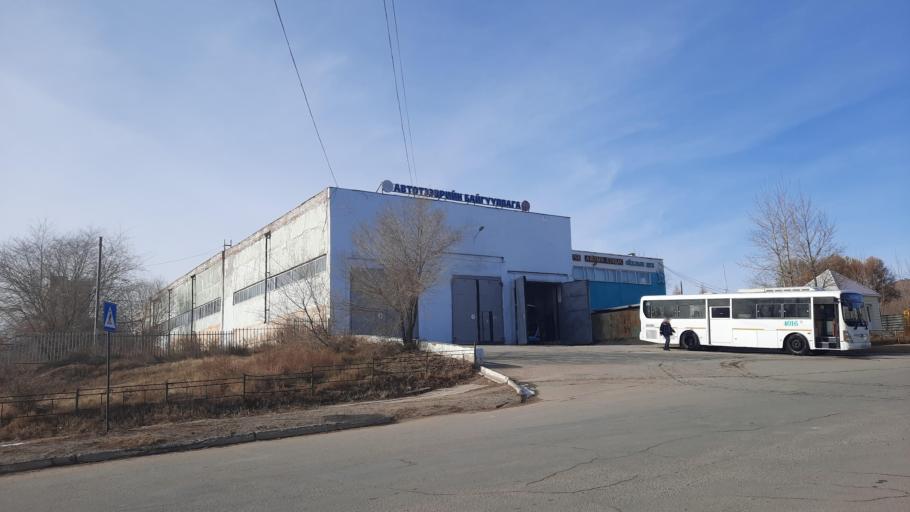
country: MN
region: Orhon
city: Erdenet
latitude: 49.0353
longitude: 104.0776
